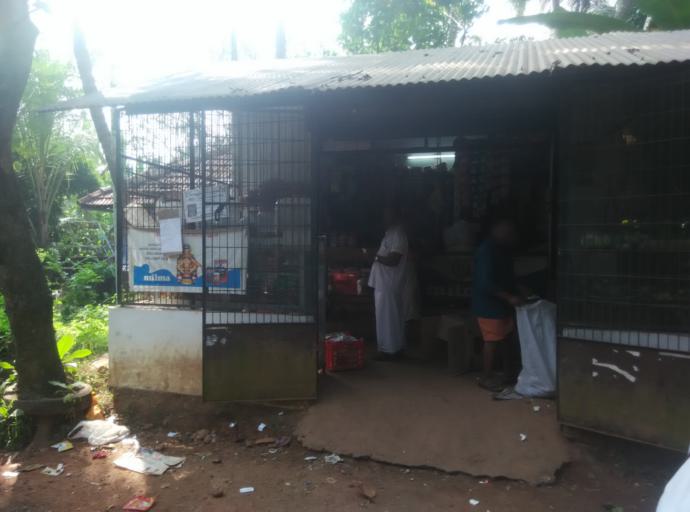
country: IN
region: Kerala
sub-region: Kozhikode
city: Kunnamangalam
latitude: 11.2856
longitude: 75.8341
